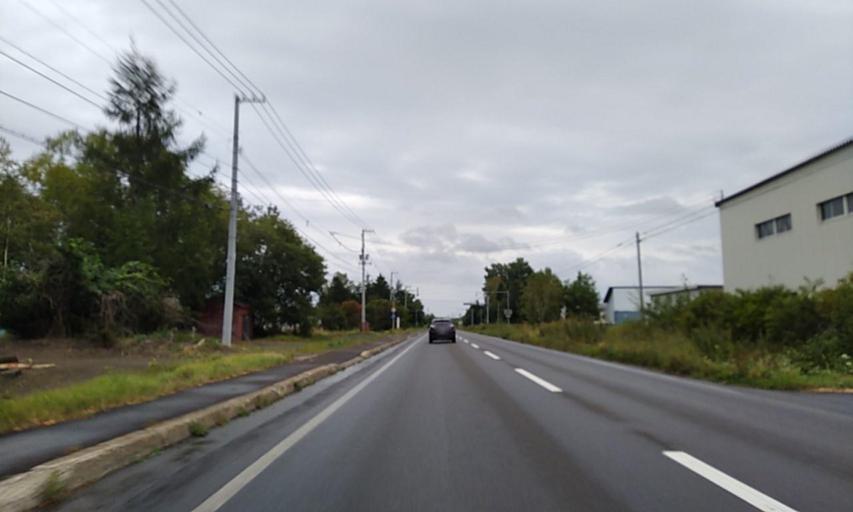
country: JP
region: Hokkaido
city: Kitami
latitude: 44.0836
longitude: 143.9476
